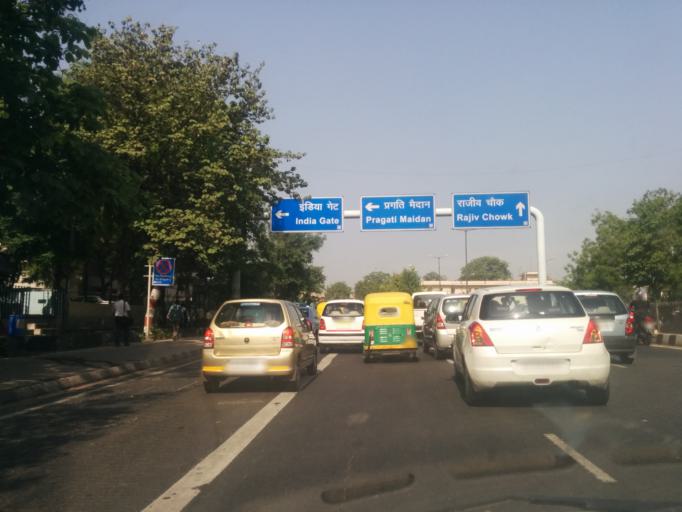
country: IN
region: NCT
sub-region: New Delhi
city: New Delhi
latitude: 28.6279
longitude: 77.2426
